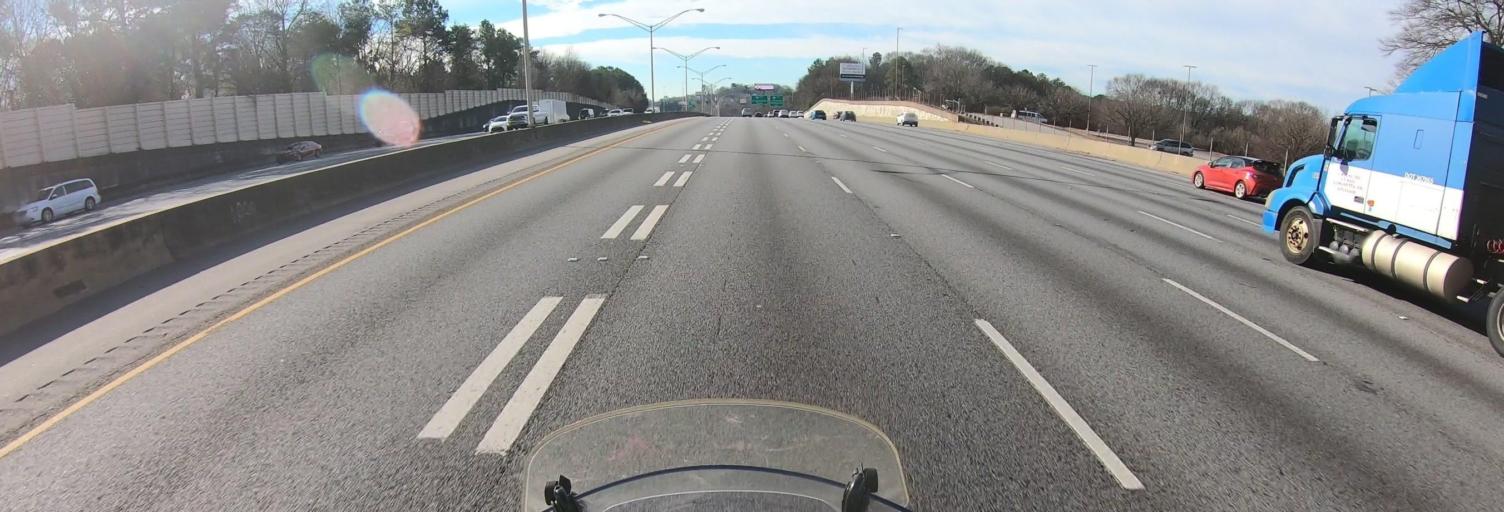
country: US
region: Georgia
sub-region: Fulton County
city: Atlanta
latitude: 33.7078
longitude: -84.4002
